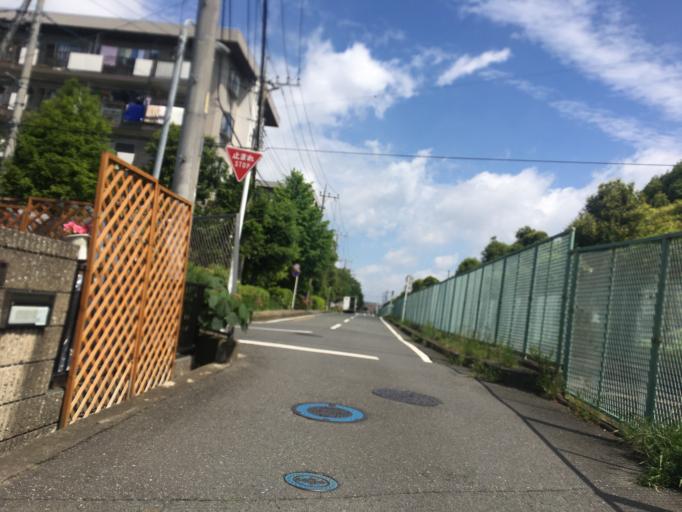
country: JP
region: Saitama
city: Yono
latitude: 35.8788
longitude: 139.6075
